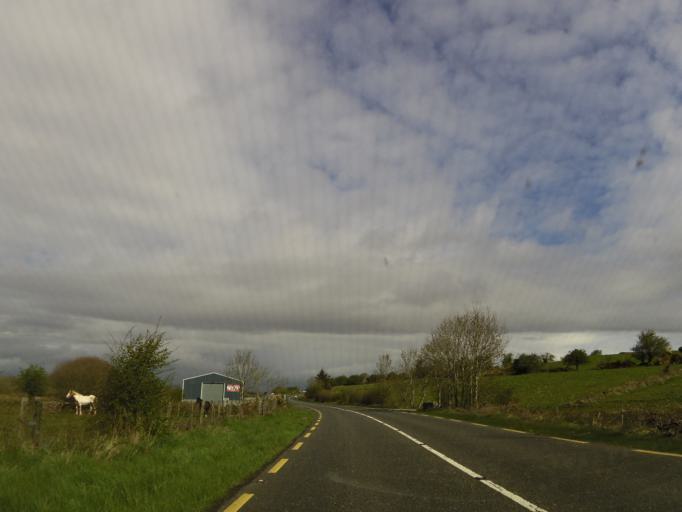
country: IE
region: Connaught
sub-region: Sligo
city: Tobercurry
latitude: 53.9453
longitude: -8.7925
